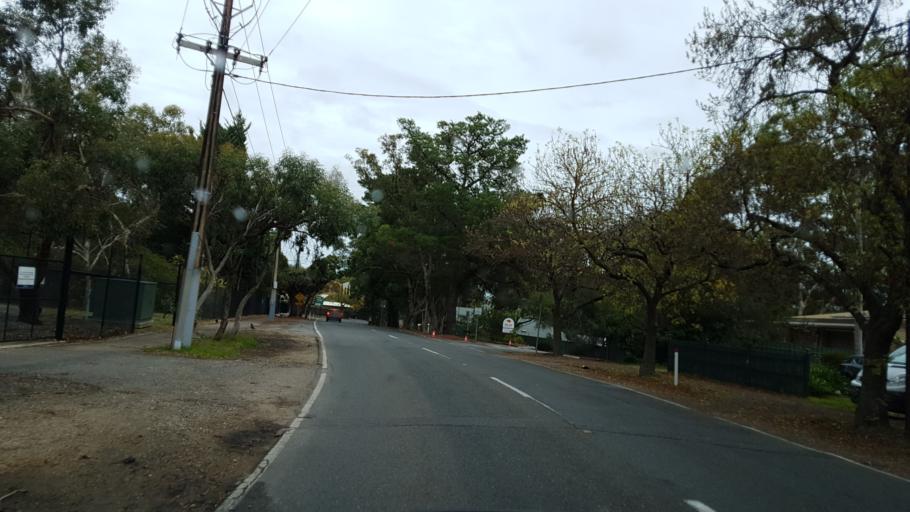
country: AU
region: South Australia
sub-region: Mitcham
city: Belair
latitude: -34.9968
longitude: 138.6269
